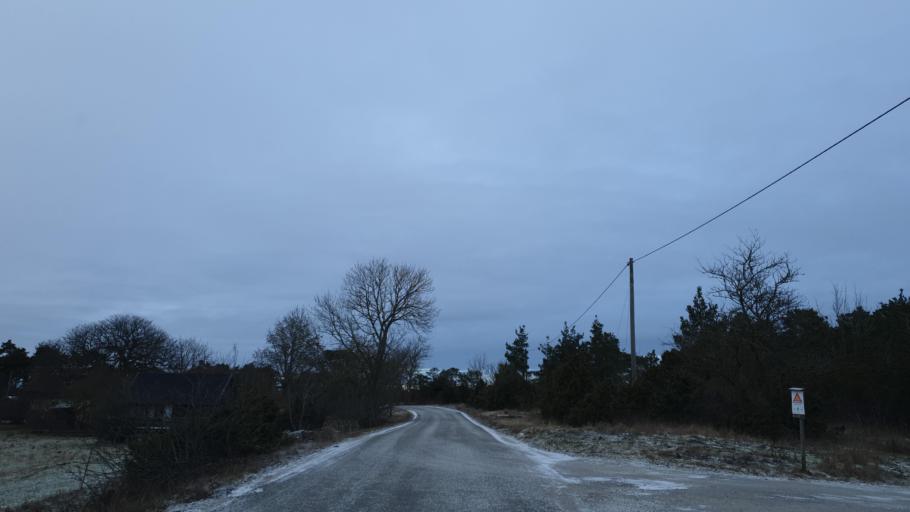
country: SE
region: Gotland
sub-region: Gotland
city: Slite
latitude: 57.3903
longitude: 18.8090
